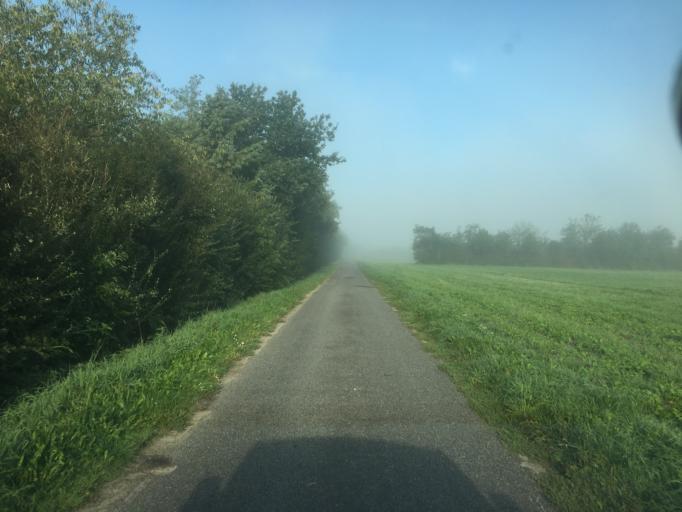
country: DK
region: South Denmark
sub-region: Tonder Kommune
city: Logumkloster
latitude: 55.0175
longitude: 8.9152
